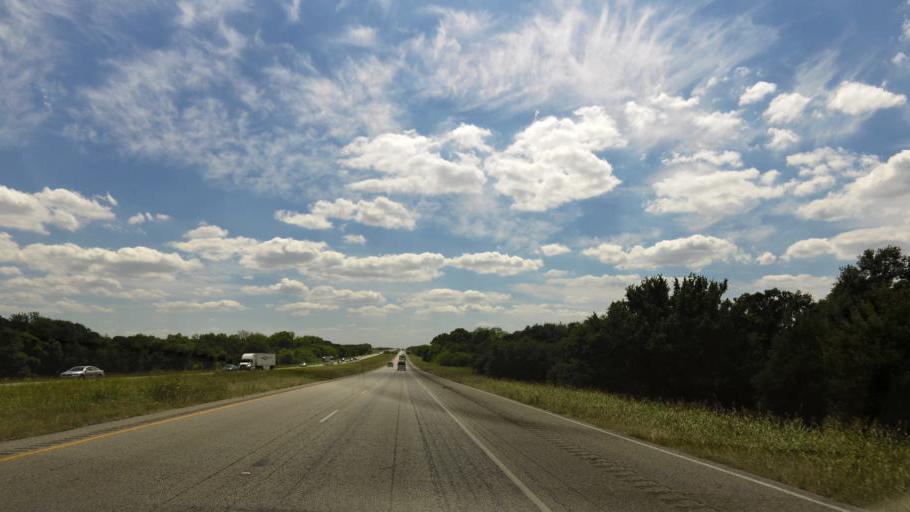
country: US
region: Texas
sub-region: Gonzales County
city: Waelder
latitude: 29.6815
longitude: -97.2715
